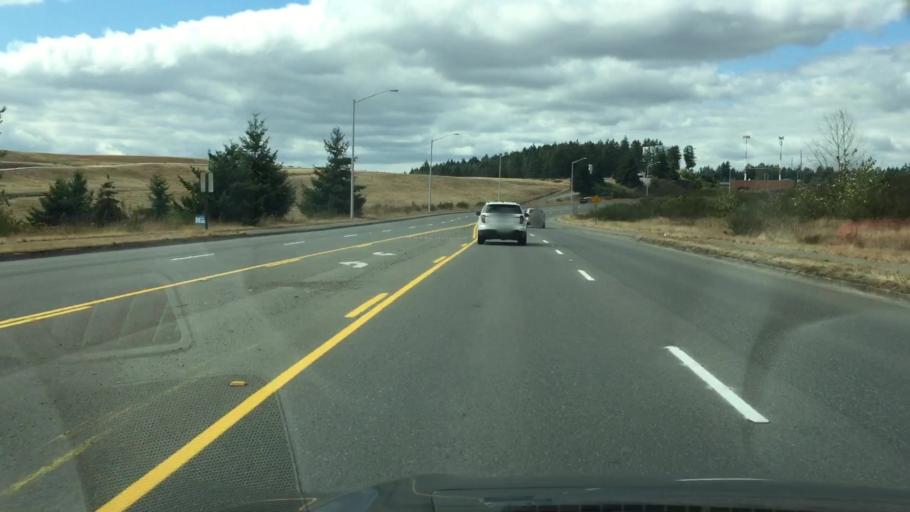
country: US
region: Washington
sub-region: Pierce County
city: Graham
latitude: 47.0976
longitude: -122.2849
